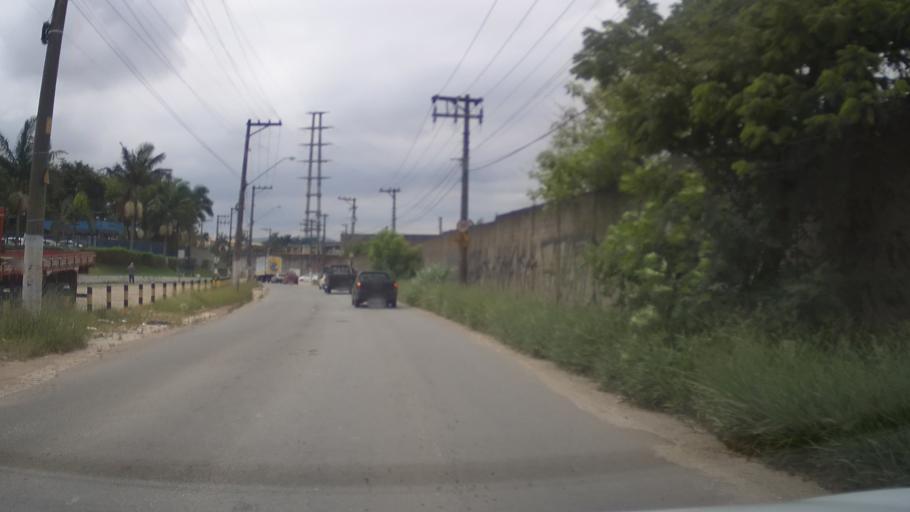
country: BR
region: Sao Paulo
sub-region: Itaquaquecetuba
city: Itaquaquecetuba
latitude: -23.4441
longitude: -46.3924
